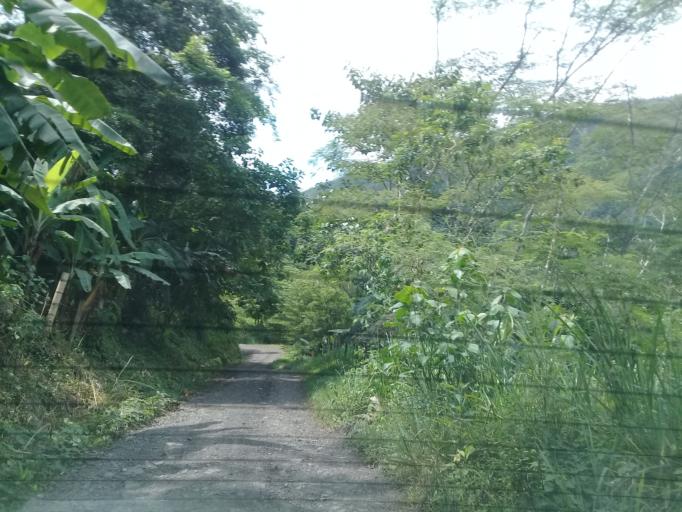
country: CO
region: Cundinamarca
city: Viani
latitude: 4.8628
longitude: -74.5396
